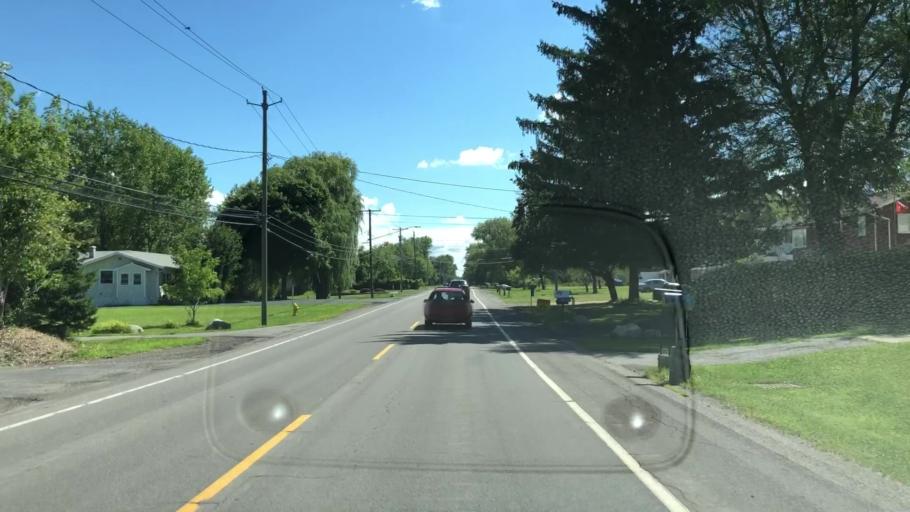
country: US
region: New York
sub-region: Erie County
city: Cheektowaga
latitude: 42.8510
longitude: -78.7401
